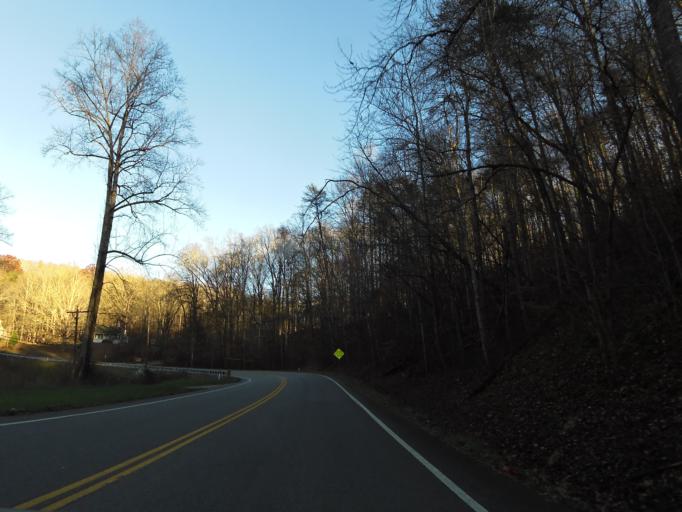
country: US
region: Tennessee
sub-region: Anderson County
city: Rocky Top
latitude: 36.2332
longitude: -84.1444
